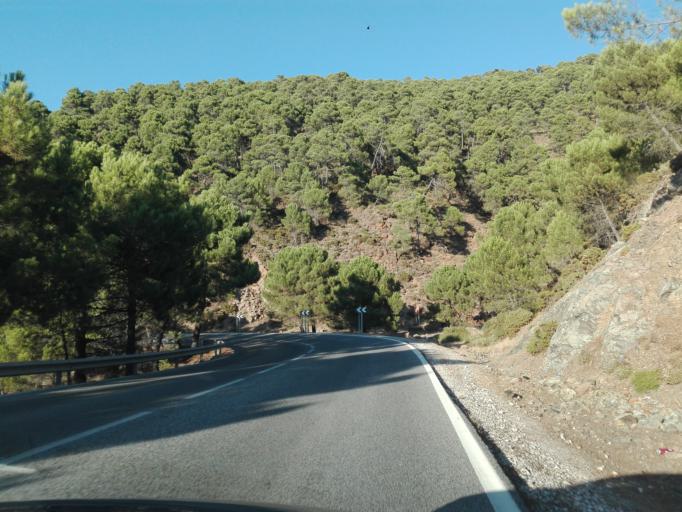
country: ES
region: Andalusia
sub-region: Provincia de Malaga
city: Igualeja
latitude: 36.6179
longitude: -5.0631
